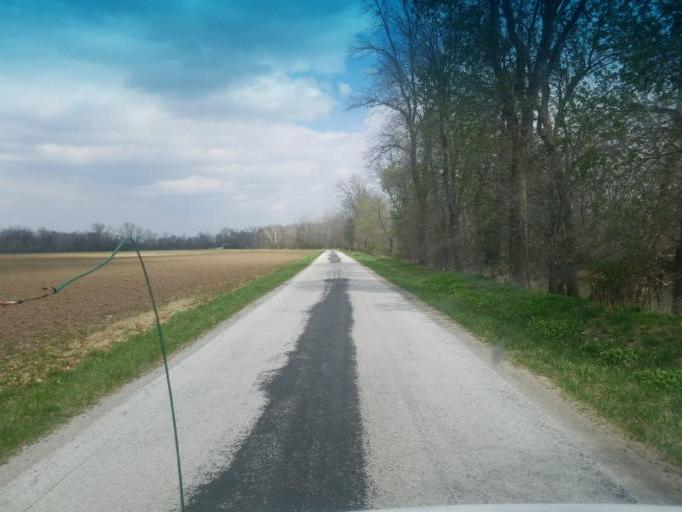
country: US
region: Ohio
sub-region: Wyandot County
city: Upper Sandusky
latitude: 40.9225
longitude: -83.2511
